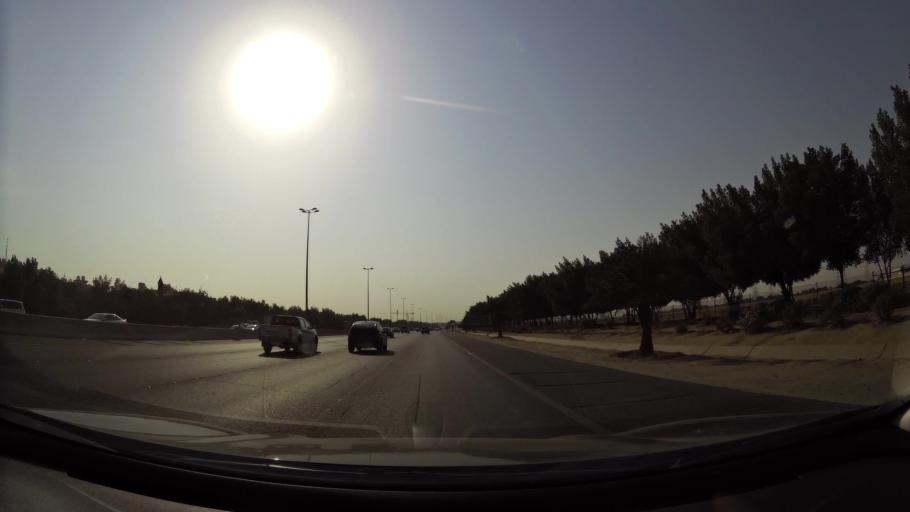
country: KW
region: Al Ahmadi
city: Ar Riqqah
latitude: 29.1404
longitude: 48.0866
